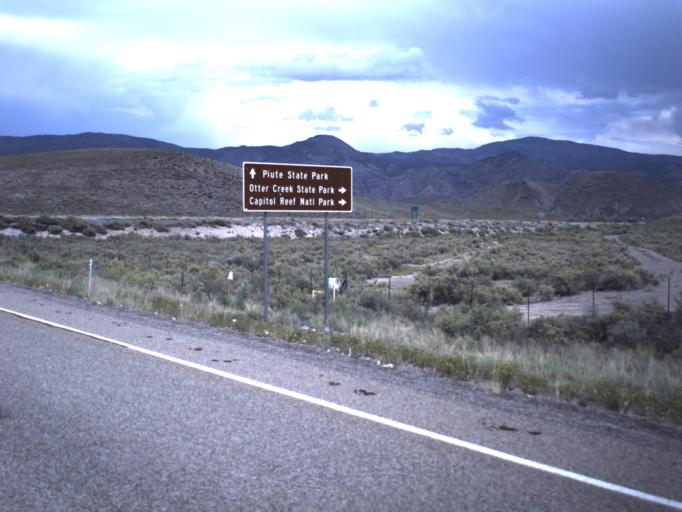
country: US
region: Utah
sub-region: Piute County
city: Junction
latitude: 38.2090
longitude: -112.2252
